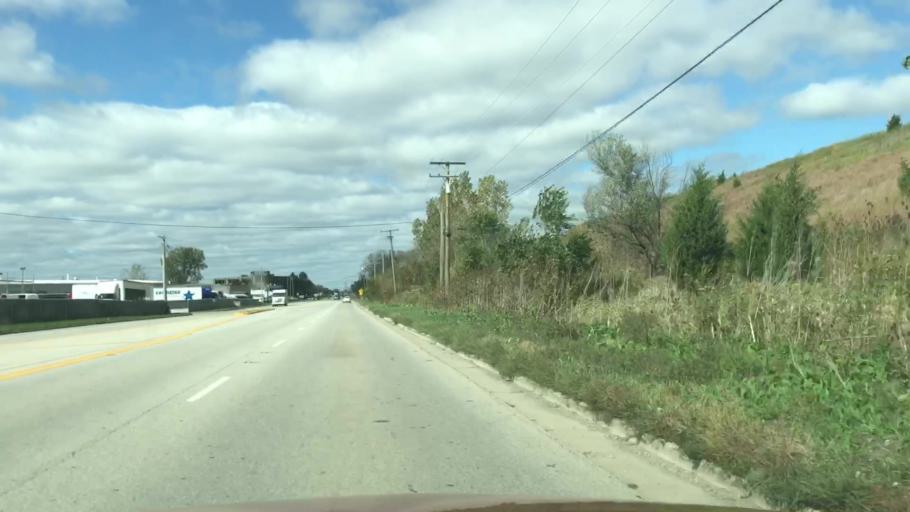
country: US
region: Illinois
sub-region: Cook County
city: Elk Grove Village
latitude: 42.0128
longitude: -87.9470
